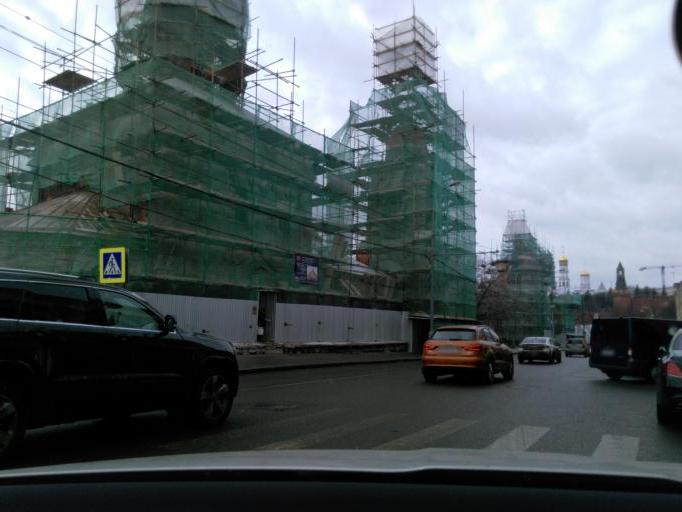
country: RU
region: Moscow
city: Moscow
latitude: 55.7529
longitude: 37.6278
